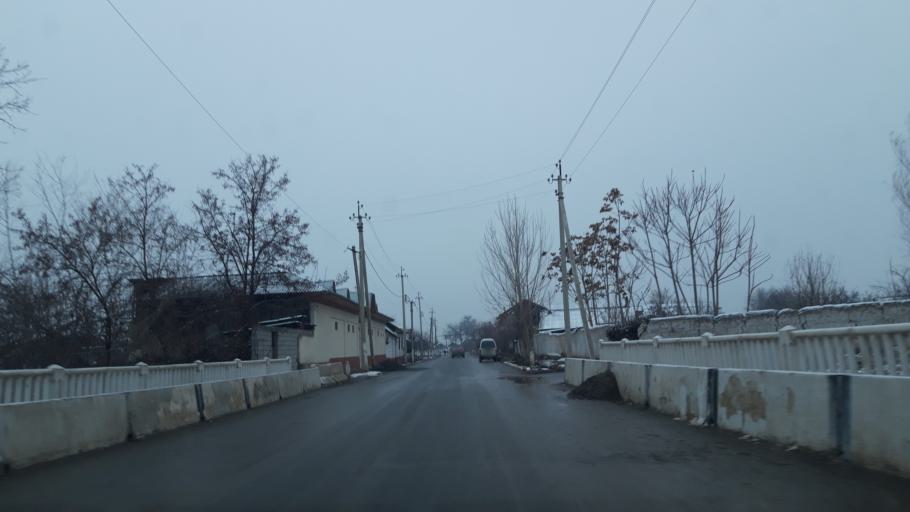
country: UZ
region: Andijon
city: Andijon
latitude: 40.7414
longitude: 72.2562
